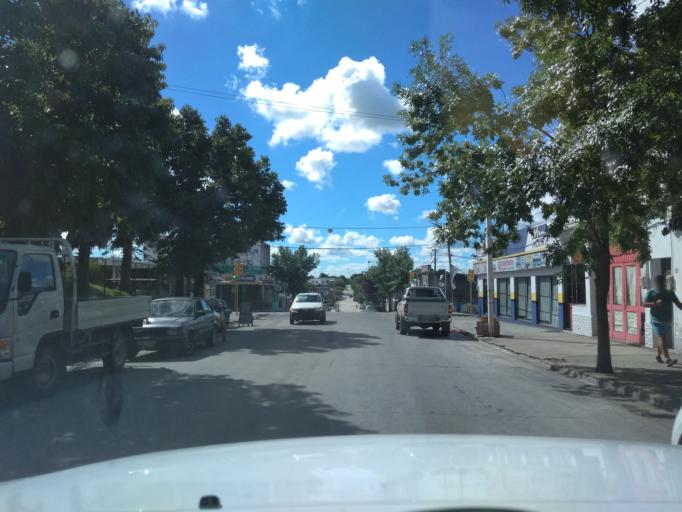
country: UY
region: Florida
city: Florida
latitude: -34.0980
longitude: -56.2083
